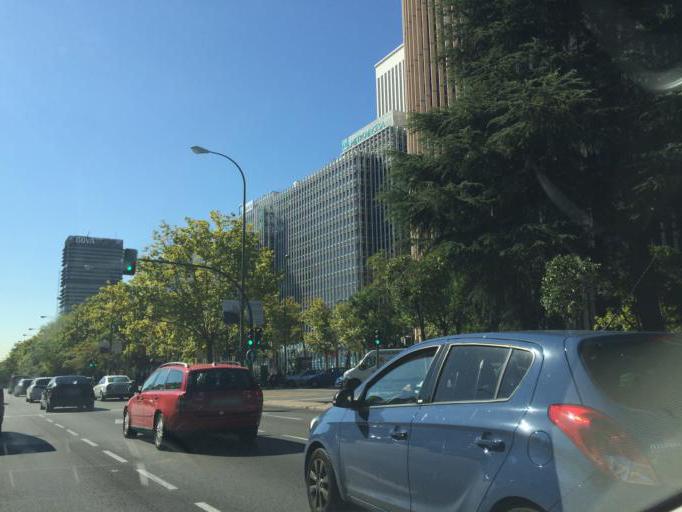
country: ES
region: Madrid
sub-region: Provincia de Madrid
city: Chamartin
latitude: 40.4521
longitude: -3.6908
